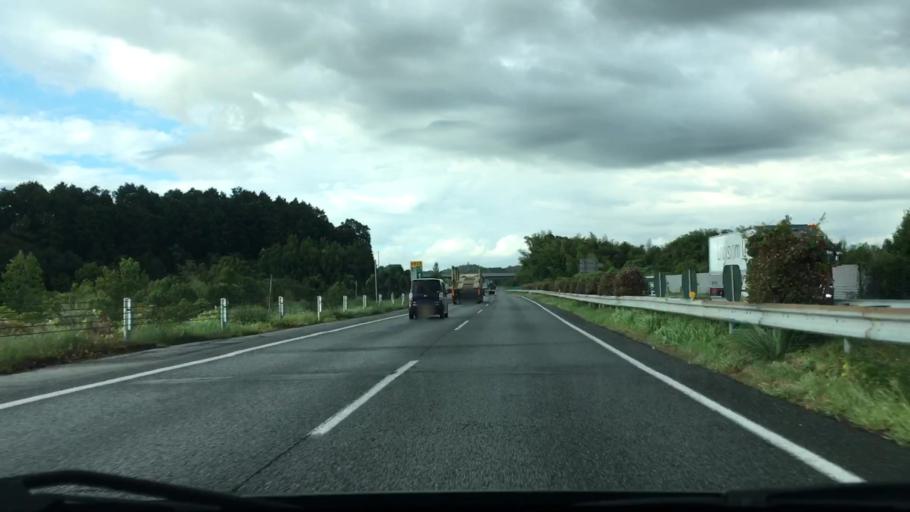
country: JP
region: Fukuoka
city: Koga
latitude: 33.7086
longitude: 130.4874
